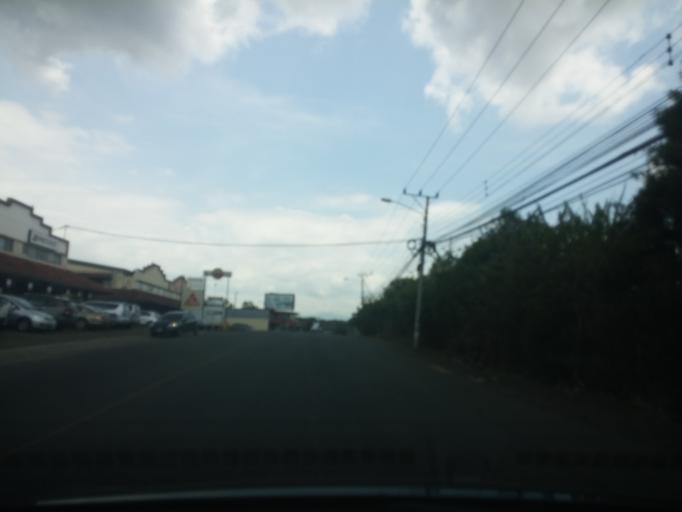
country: CR
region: Heredia
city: San Francisco
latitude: 9.9760
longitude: -84.1426
